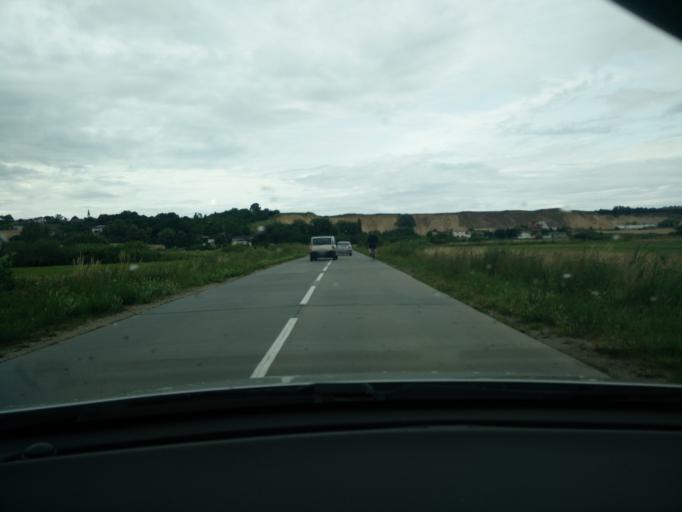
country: PL
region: Pomeranian Voivodeship
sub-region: Powiat pucki
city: Mrzezino
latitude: 54.6439
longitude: 18.4366
